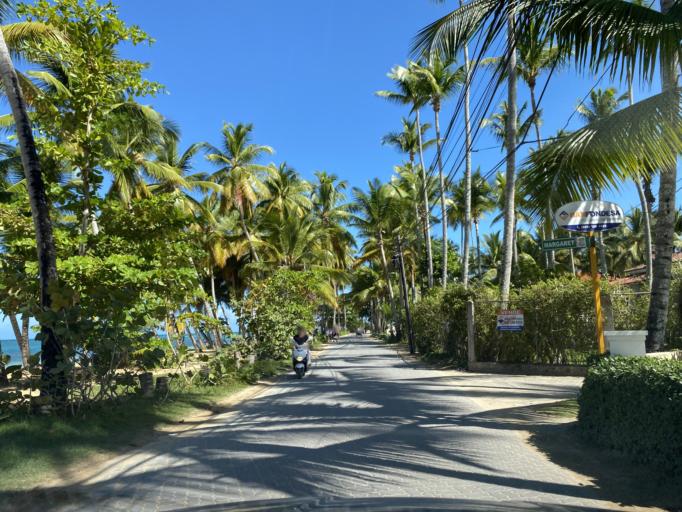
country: DO
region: Samana
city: Las Terrenas
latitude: 19.3262
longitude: -69.5473
